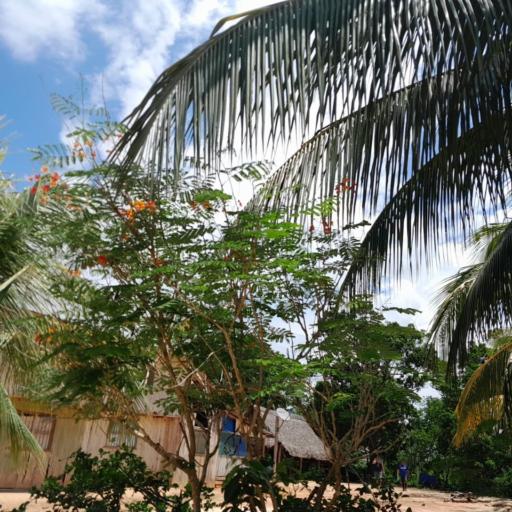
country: PE
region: Ucayali
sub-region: Provincia de Coronel Portillo
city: Puerto Callao
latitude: -8.2710
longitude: -74.6495
